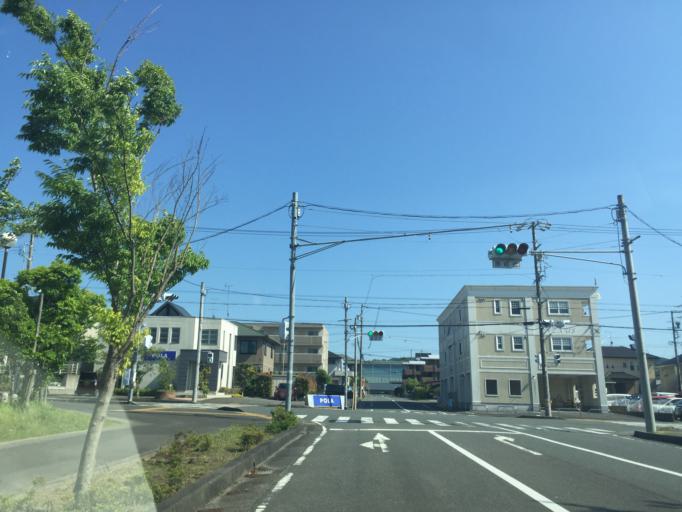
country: JP
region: Shizuoka
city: Kakegawa
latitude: 34.7675
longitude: 137.9959
